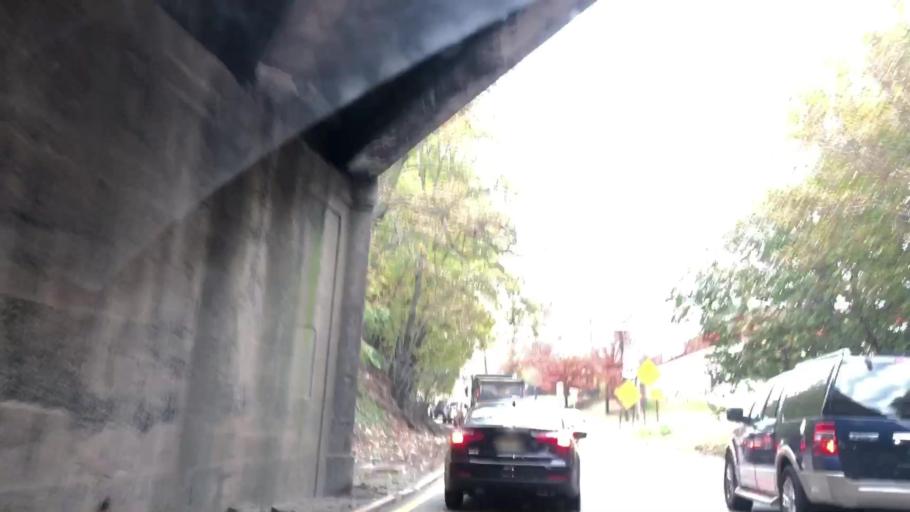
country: US
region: New Jersey
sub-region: Passaic County
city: Woodland Park
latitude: 40.8701
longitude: -74.1867
